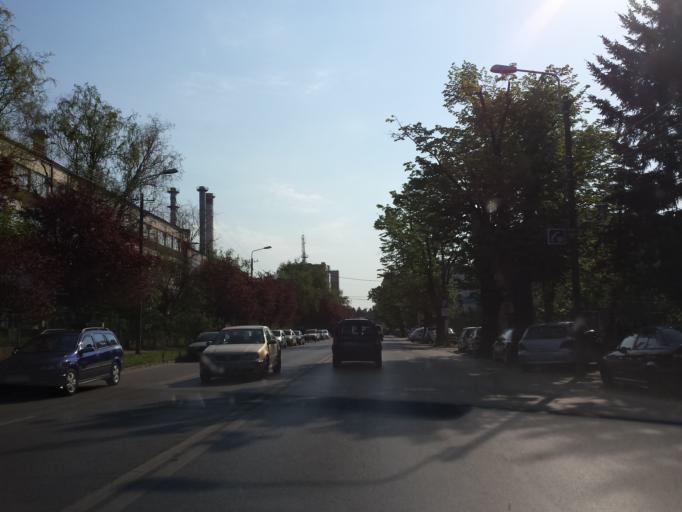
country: RO
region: Timis
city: Timisoara
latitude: 45.7545
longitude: 21.2446
